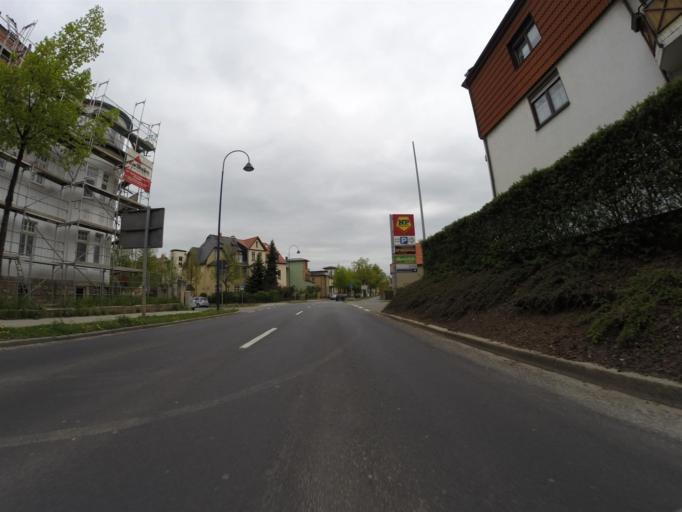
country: DE
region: Saxony-Anhalt
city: Naumburg
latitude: 51.1486
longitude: 11.8012
